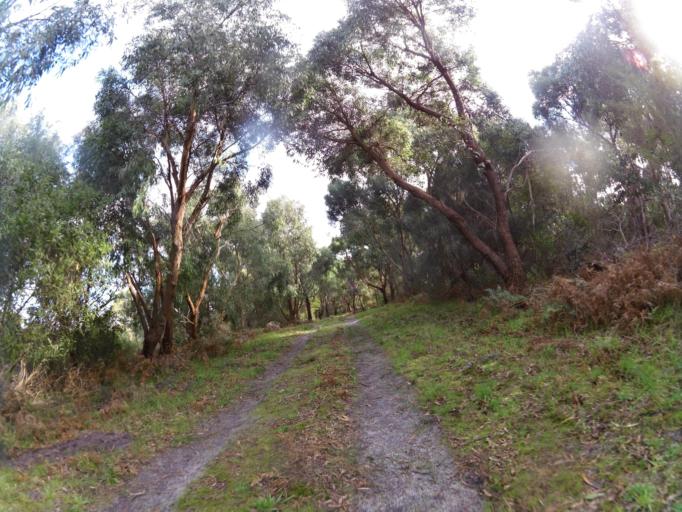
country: AU
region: Victoria
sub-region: Bass Coast
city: North Wonthaggi
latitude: -38.6242
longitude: 145.5728
